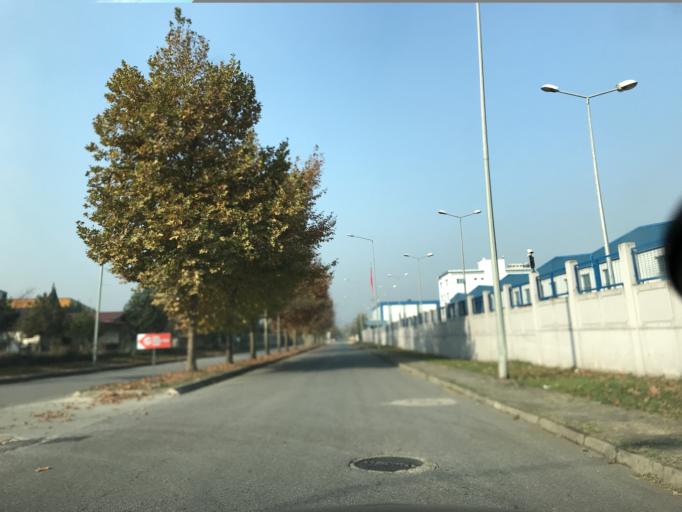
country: TR
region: Duzce
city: Duzce
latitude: 40.7877
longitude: 31.1360
